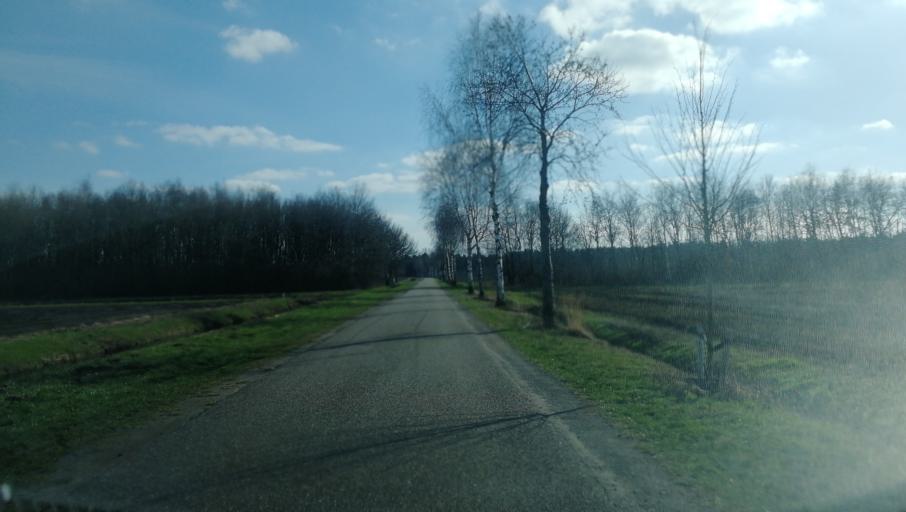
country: NL
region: Limburg
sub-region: Gemeente Peel en Maas
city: Maasbree
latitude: 51.3987
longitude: 5.9762
